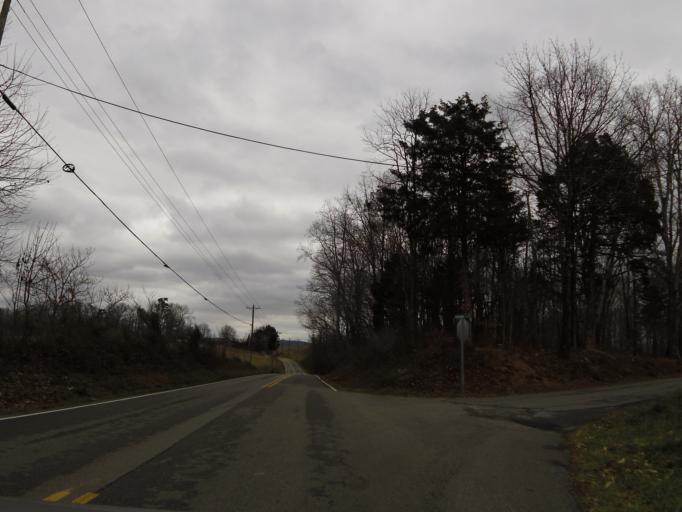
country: US
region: Tennessee
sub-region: Jefferson County
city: New Market
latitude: 36.1733
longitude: -83.6018
